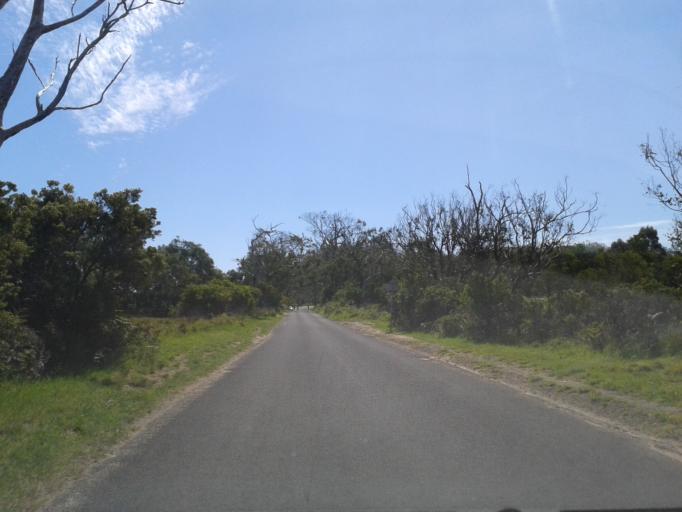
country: AU
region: Victoria
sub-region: Colac-Otway
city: Apollo Bay
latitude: -38.8330
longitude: 143.5215
